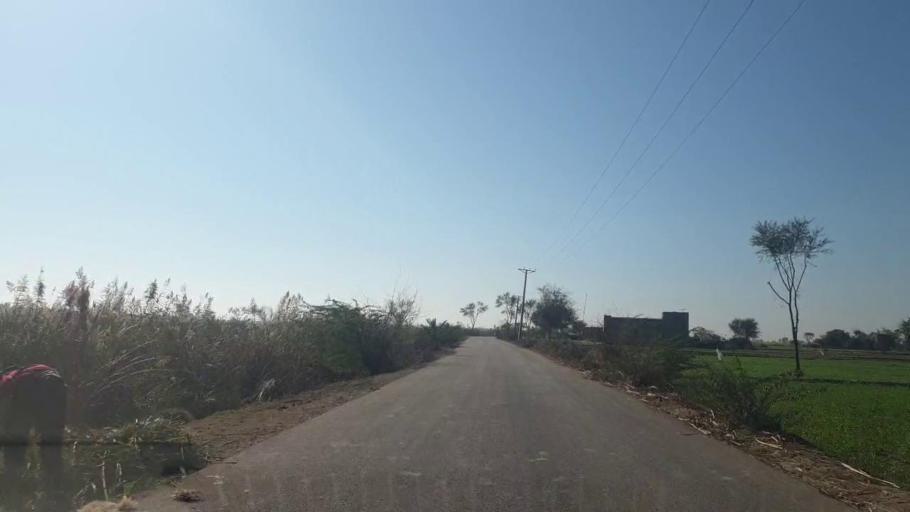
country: PK
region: Sindh
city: Kot Diji
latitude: 27.3114
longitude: 68.6479
